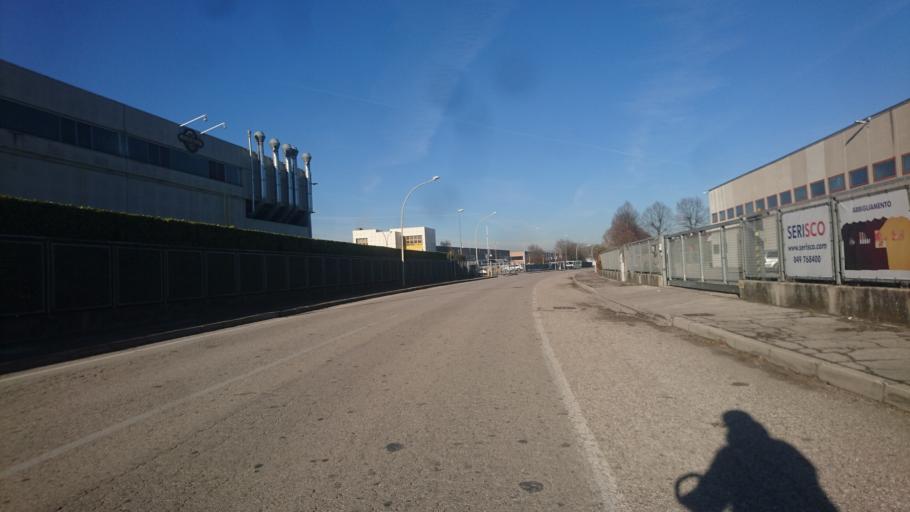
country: IT
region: Veneto
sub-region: Provincia di Padova
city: Limena
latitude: 45.4585
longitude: 11.8484
